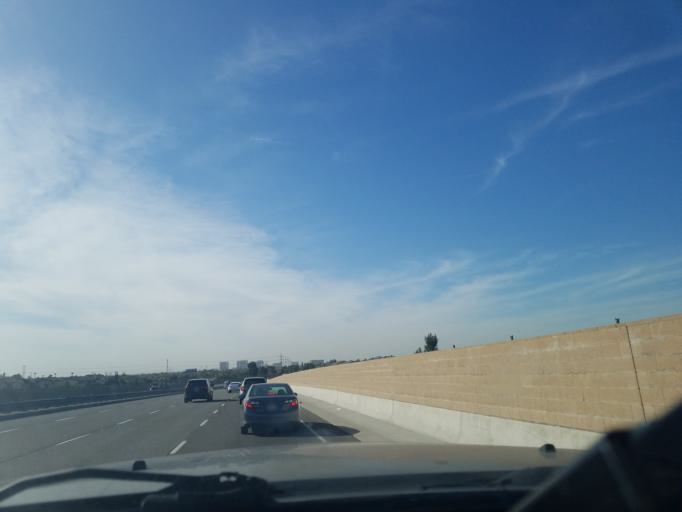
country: US
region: California
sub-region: Orange County
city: Irvine
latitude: 33.7007
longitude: -117.8107
